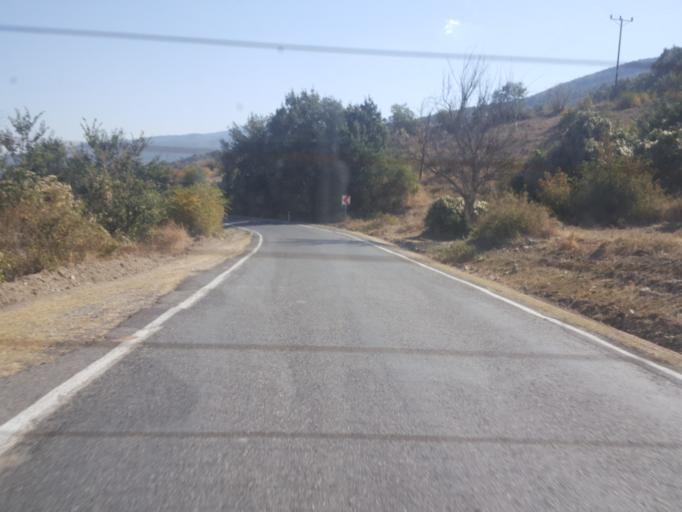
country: TR
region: Kastamonu
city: Tosya
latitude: 40.9925
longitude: 34.1257
